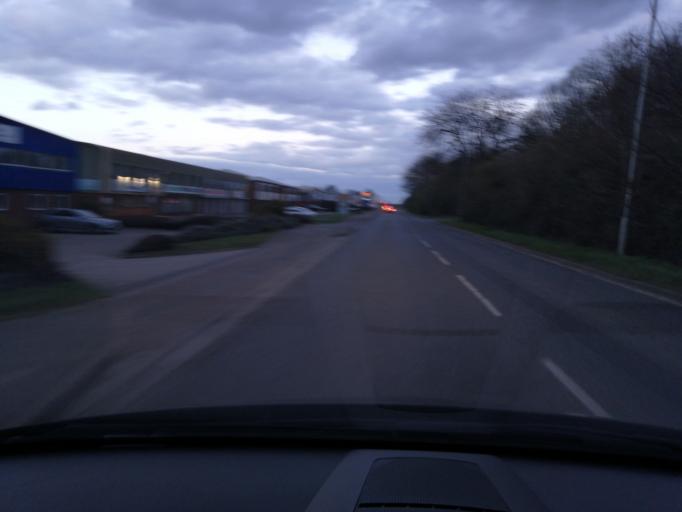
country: GB
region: England
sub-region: Peterborough
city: Eye
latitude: 52.5766
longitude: -0.2069
